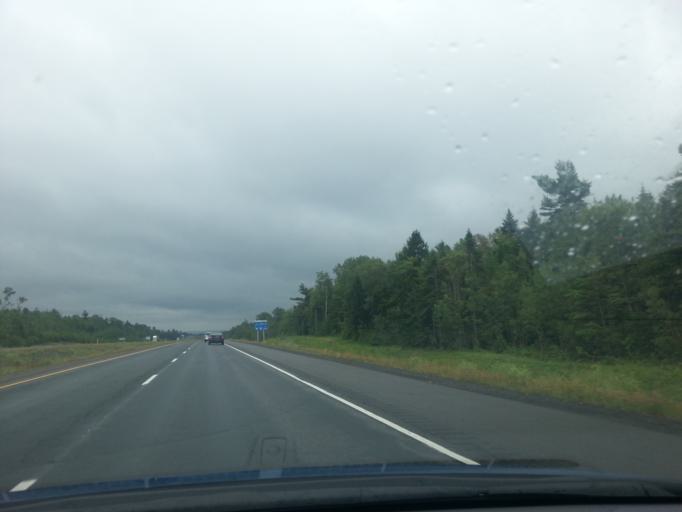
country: CA
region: New Brunswick
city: Fredericton
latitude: 45.9139
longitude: -66.6913
